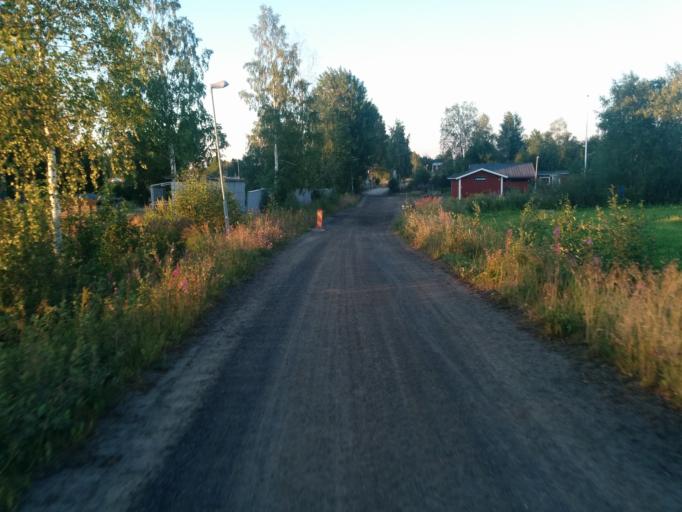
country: SE
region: Vaesterbotten
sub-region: Umea Kommun
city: Ersmark
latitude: 63.8538
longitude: 20.3834
